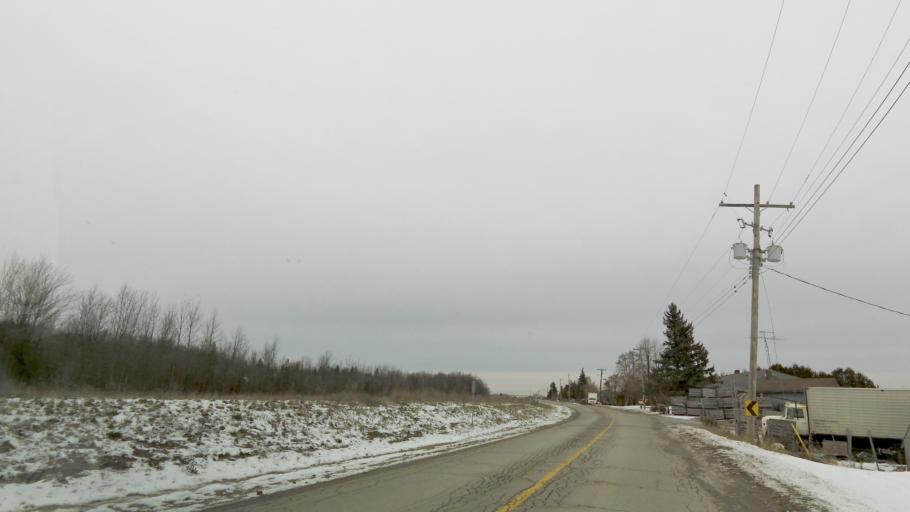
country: CA
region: Ontario
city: Bradford West Gwillimbury
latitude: 44.0609
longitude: -79.5940
